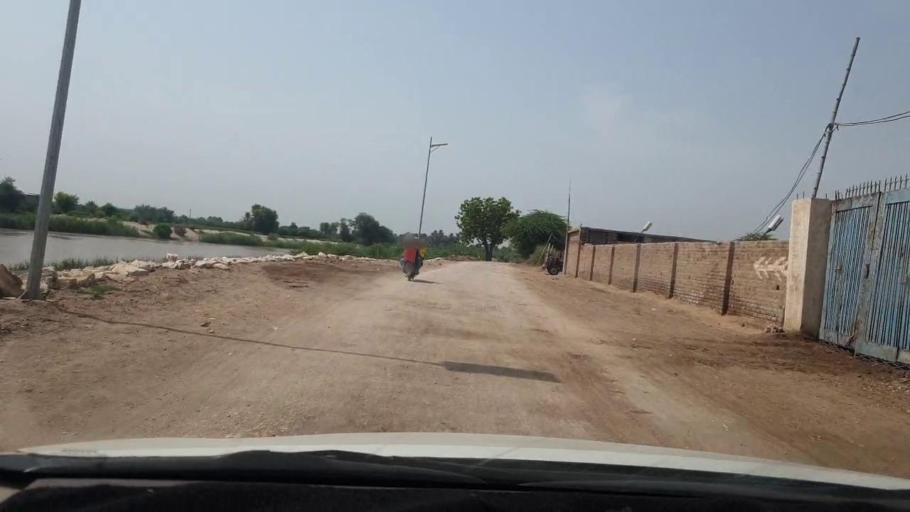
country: PK
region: Sindh
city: Rohri
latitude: 27.5372
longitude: 69.0314
